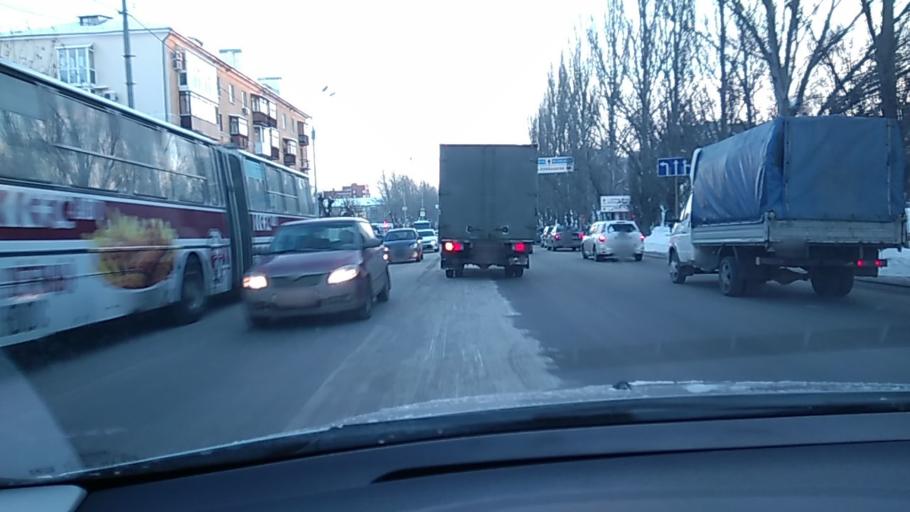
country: RU
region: Sverdlovsk
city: Yekaterinburg
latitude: 56.8318
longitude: 60.6357
